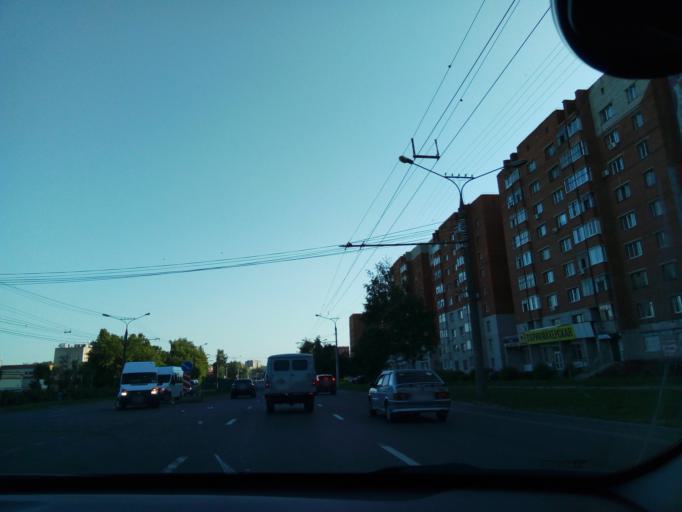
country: RU
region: Chuvashia
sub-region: Cheboksarskiy Rayon
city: Cheboksary
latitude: 56.1148
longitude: 47.2725
